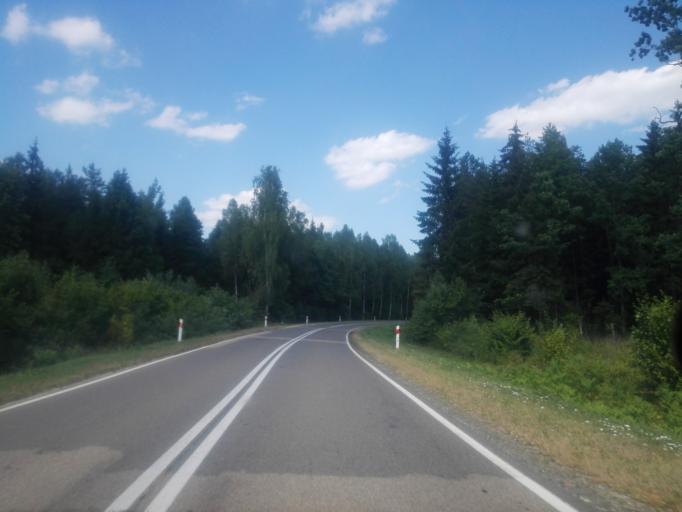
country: PL
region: Podlasie
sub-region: Powiat sejnenski
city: Sejny
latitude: 54.0090
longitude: 23.3248
